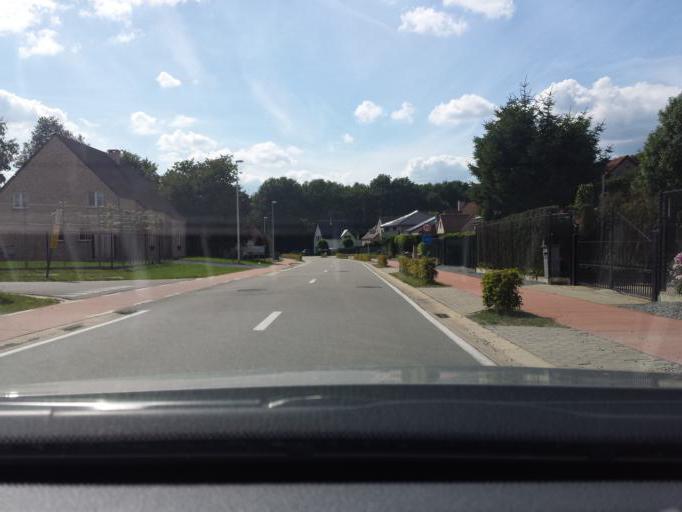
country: BE
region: Flanders
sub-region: Provincie Limburg
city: Lummen
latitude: 50.9909
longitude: 5.2231
